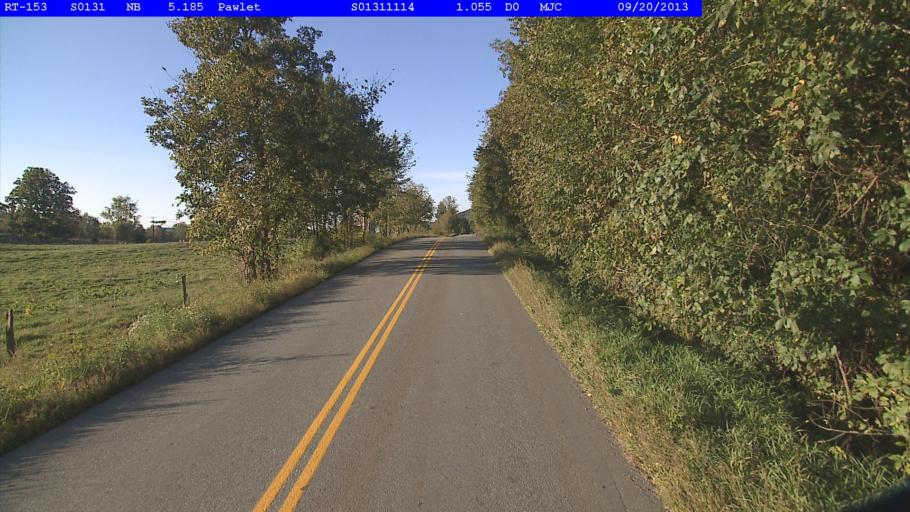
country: US
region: New York
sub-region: Washington County
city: Granville
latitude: 43.3291
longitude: -73.2435
